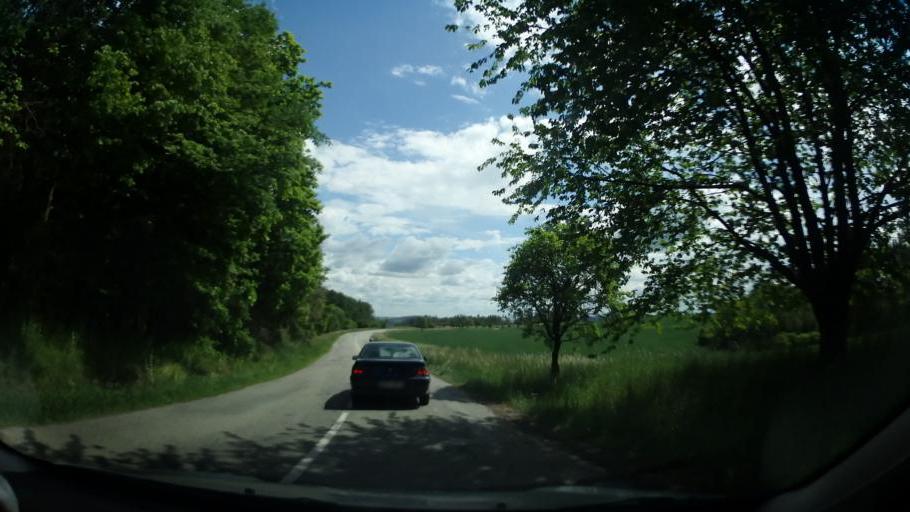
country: CZ
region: South Moravian
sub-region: Okres Blansko
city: Letovice
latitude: 49.5784
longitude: 16.5843
